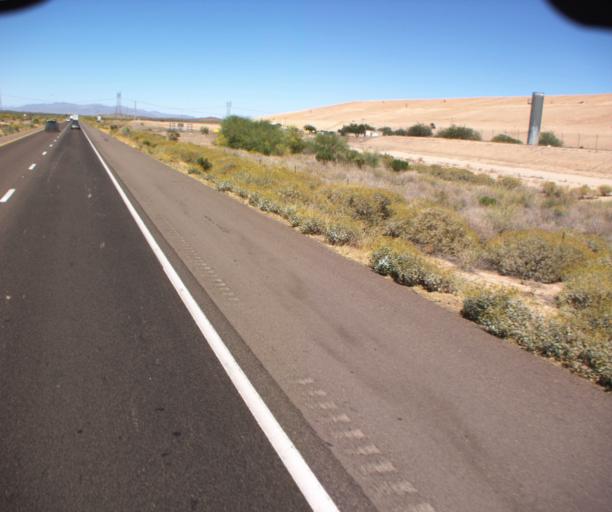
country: US
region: Arizona
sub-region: Maricopa County
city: Buckeye
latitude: 33.2203
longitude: -112.6437
